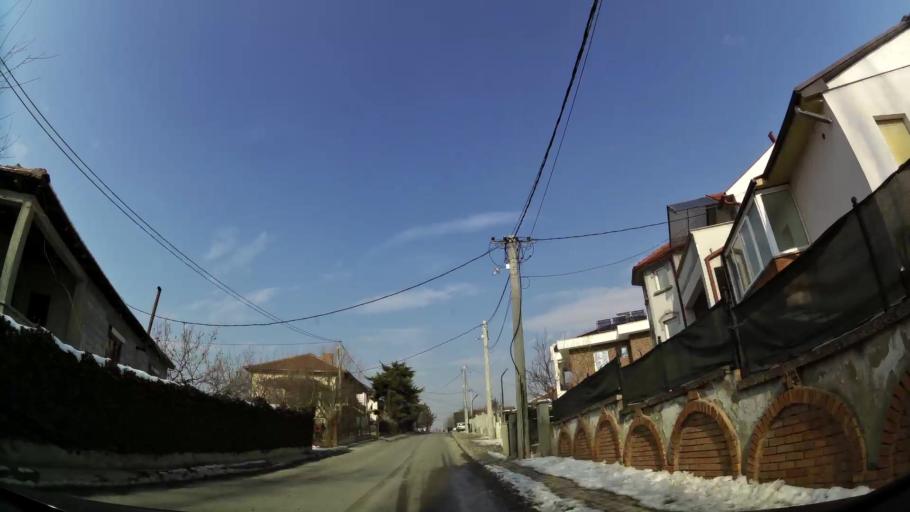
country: MK
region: Suto Orizari
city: Suto Orizare
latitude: 42.0258
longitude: 21.3792
